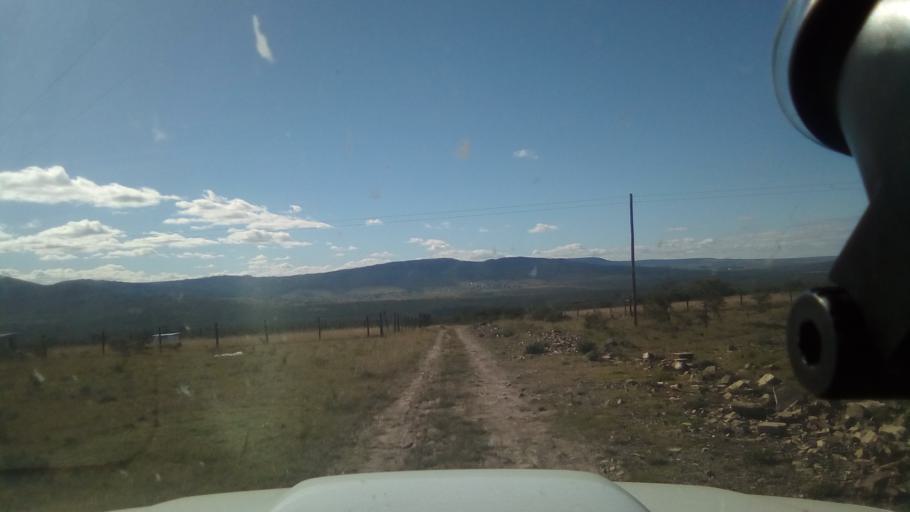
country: ZA
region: Eastern Cape
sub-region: Buffalo City Metropolitan Municipality
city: Bhisho
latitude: -32.7793
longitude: 27.3358
